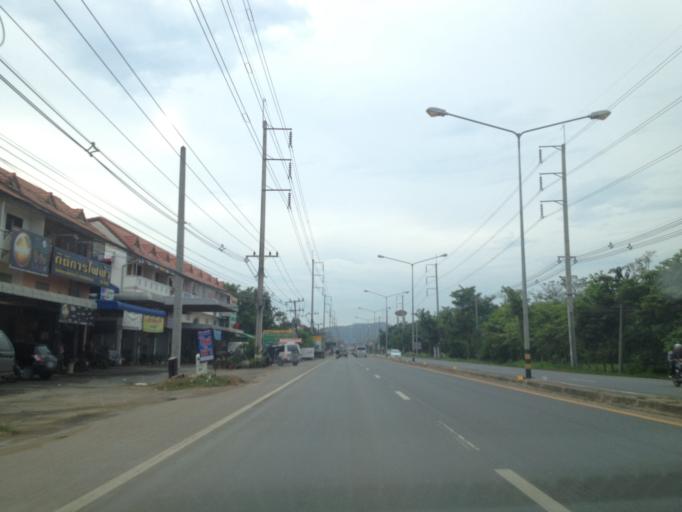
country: TH
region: Chiang Mai
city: Hang Dong
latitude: 18.7238
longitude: 98.9351
